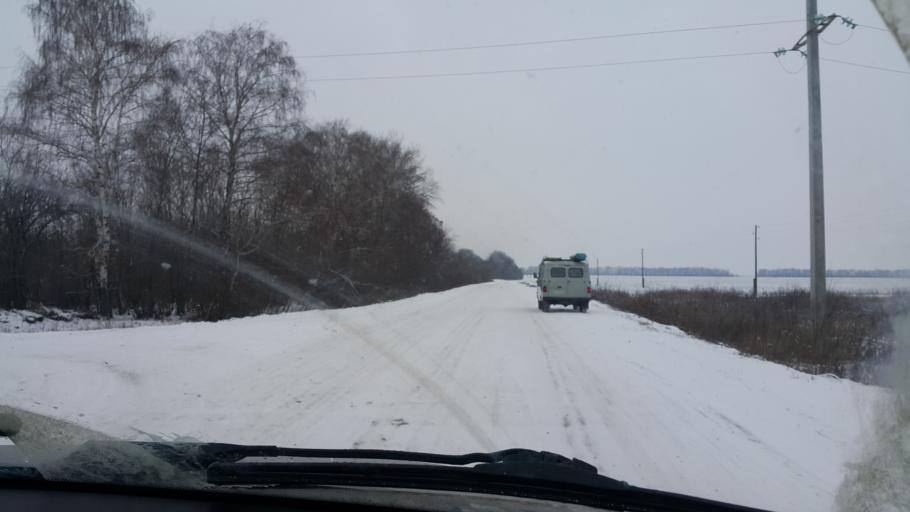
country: RU
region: Tambov
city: Inzhavino
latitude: 52.4695
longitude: 42.3826
